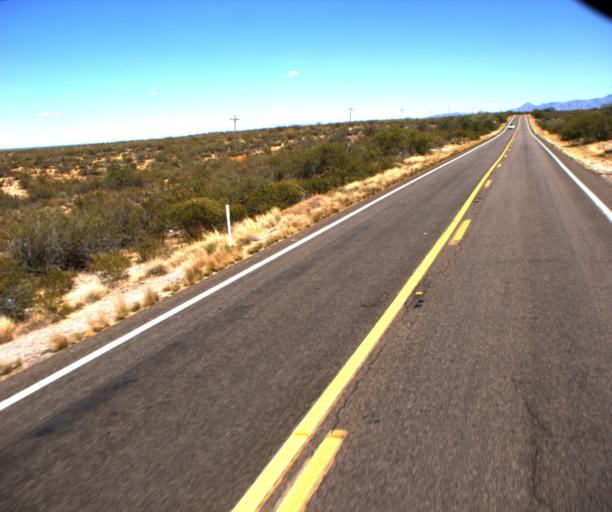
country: US
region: Arizona
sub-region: Pima County
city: Catalina
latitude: 32.6483
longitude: -111.0271
